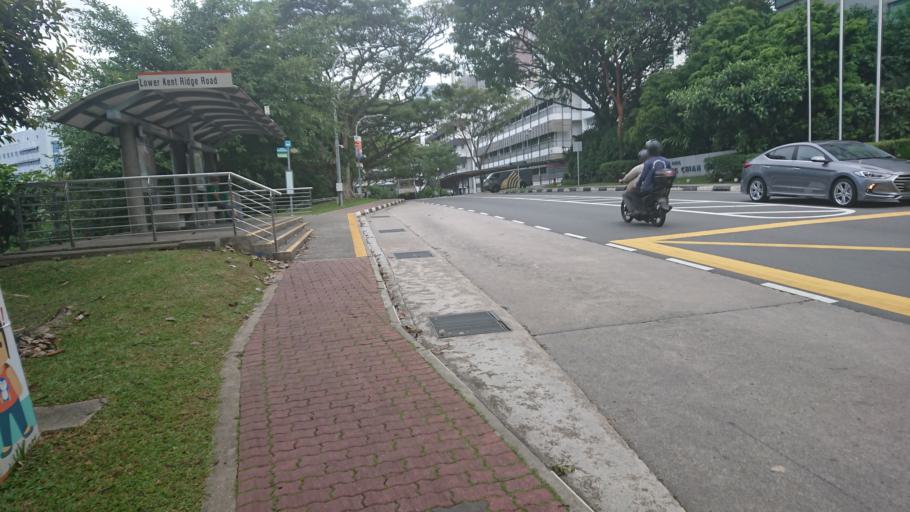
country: SG
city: Singapore
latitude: 1.2976
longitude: 103.7779
